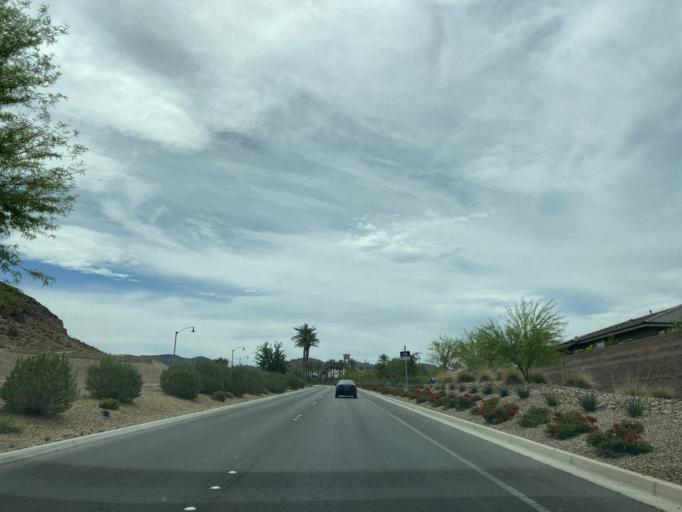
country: US
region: Nevada
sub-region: Clark County
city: Henderson
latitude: 36.0904
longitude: -114.9329
